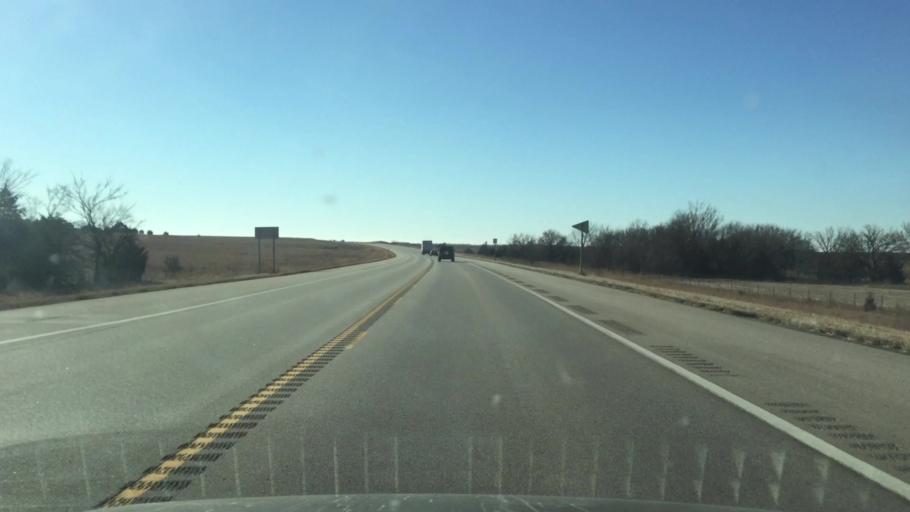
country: US
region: Kansas
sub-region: Allen County
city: Iola
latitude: 38.0665
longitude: -95.3796
